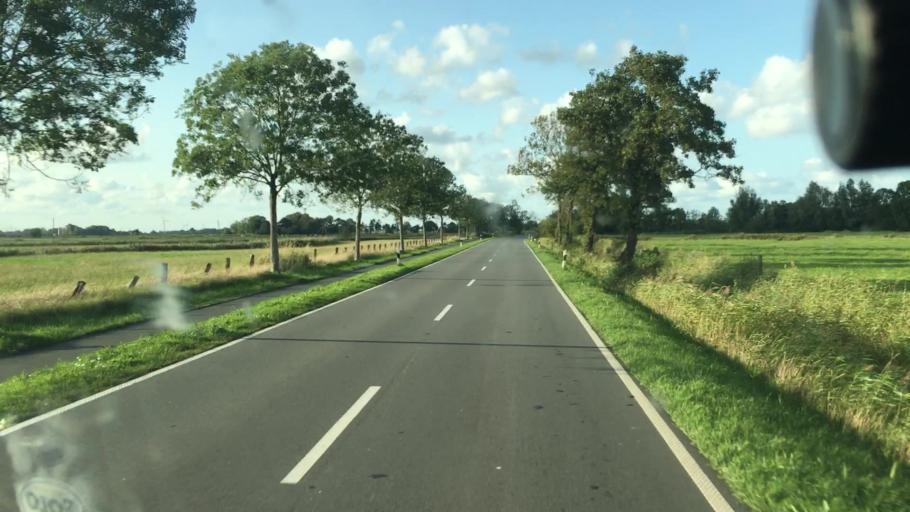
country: DE
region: Lower Saxony
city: Jever
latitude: 53.6022
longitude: 7.8697
